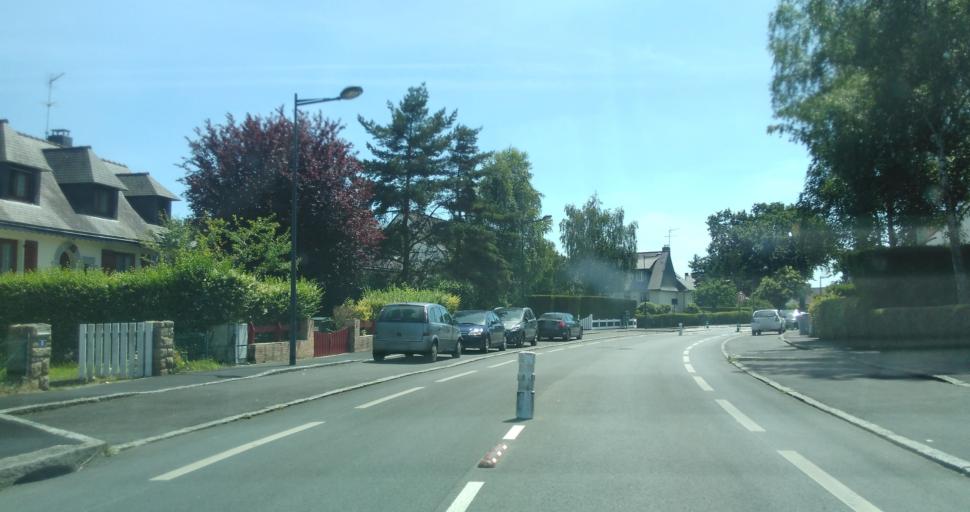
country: FR
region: Brittany
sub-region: Departement d'Ille-et-Vilaine
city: Chantepie
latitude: 48.0903
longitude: -1.6078
